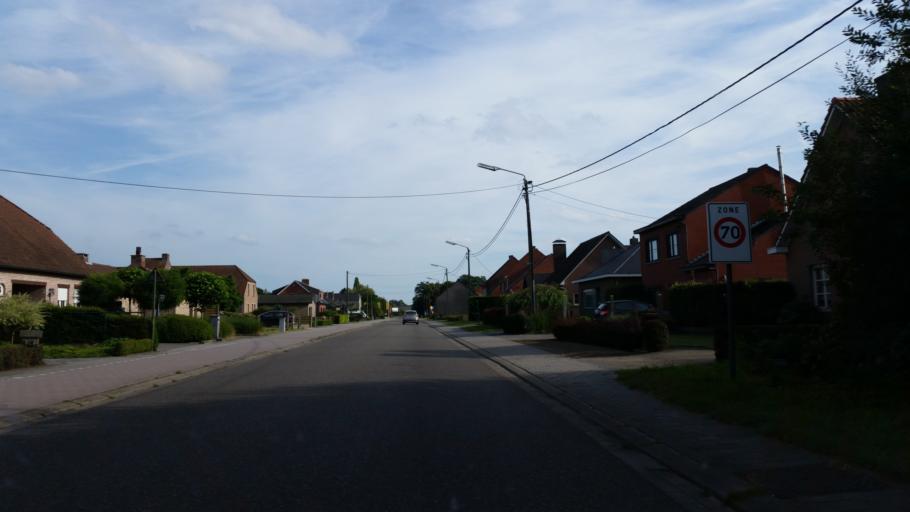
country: BE
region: Flanders
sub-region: Provincie Antwerpen
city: Westerlo
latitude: 51.1172
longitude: 4.9105
